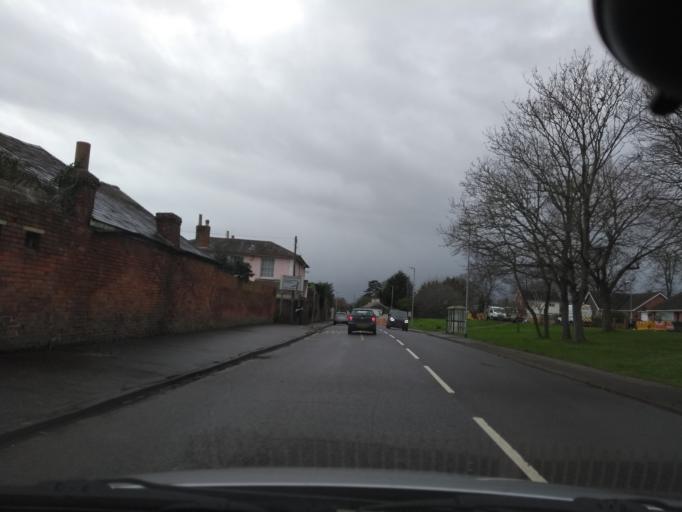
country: GB
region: England
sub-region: Somerset
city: Taunton
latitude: 51.0287
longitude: -3.1187
